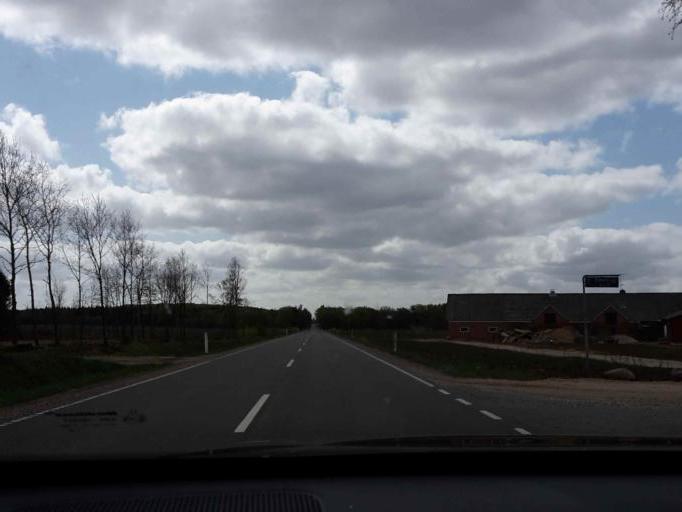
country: DK
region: South Denmark
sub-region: Varde Kommune
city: Olgod
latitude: 55.7040
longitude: 8.6073
